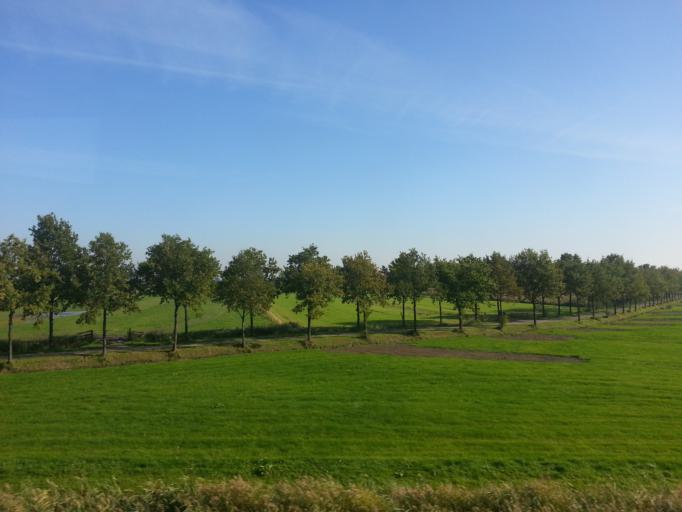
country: NL
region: Gelderland
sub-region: Gemeente Culemborg
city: Culemborg
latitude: 51.9703
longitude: 5.2043
